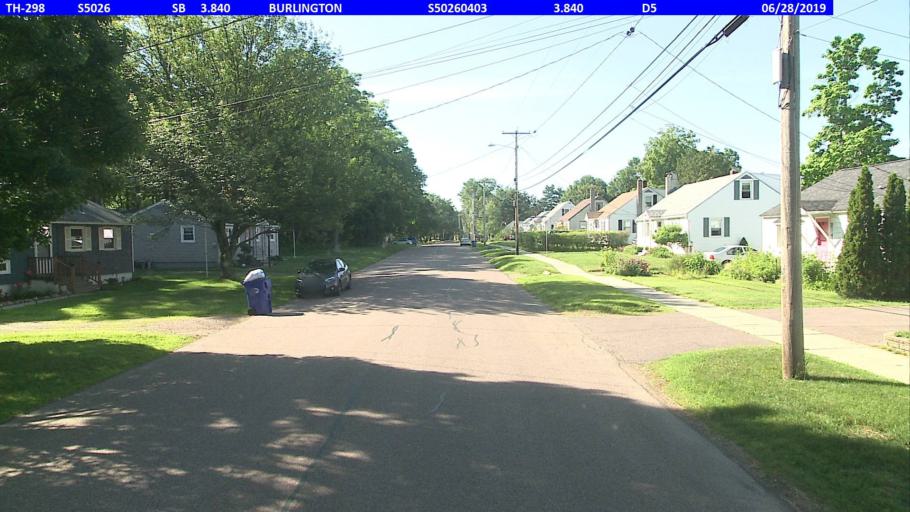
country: US
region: Vermont
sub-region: Chittenden County
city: Burlington
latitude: 44.5239
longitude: -73.2662
